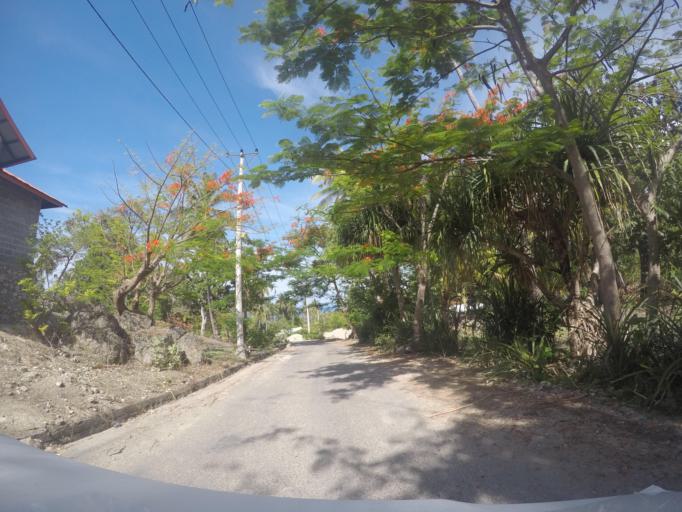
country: TL
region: Baucau
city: Baucau
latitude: -8.4578
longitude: 126.4574
